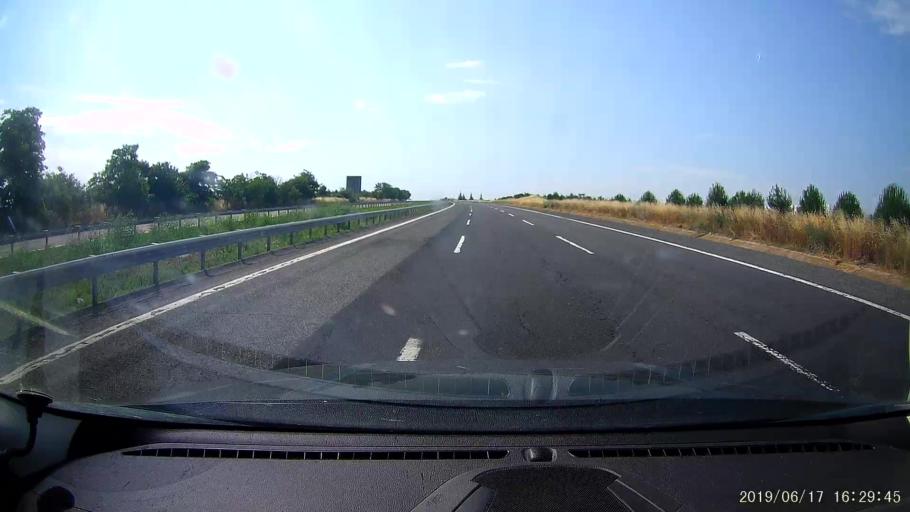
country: TR
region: Tekirdag
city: Beyazkoy
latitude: 41.3379
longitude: 27.6732
